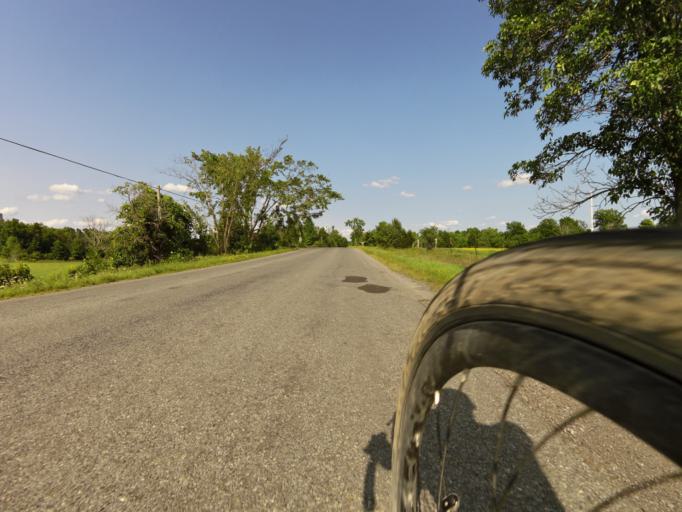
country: CA
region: Ontario
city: Kingston
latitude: 44.3439
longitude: -76.6551
